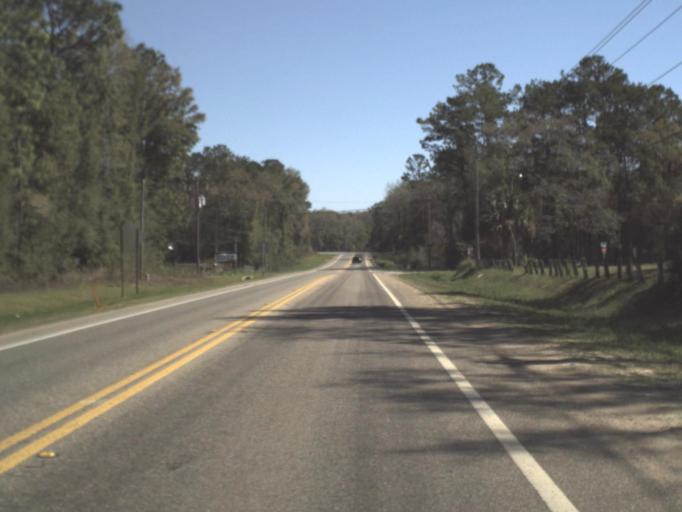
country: US
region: Florida
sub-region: Leon County
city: Tallahassee
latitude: 30.3787
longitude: -84.3013
